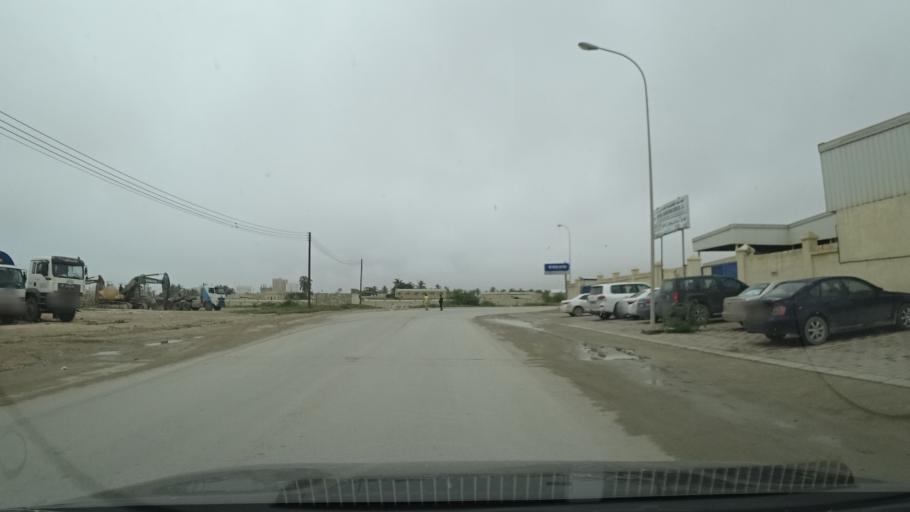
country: OM
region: Zufar
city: Salalah
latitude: 17.0120
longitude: 54.0452
